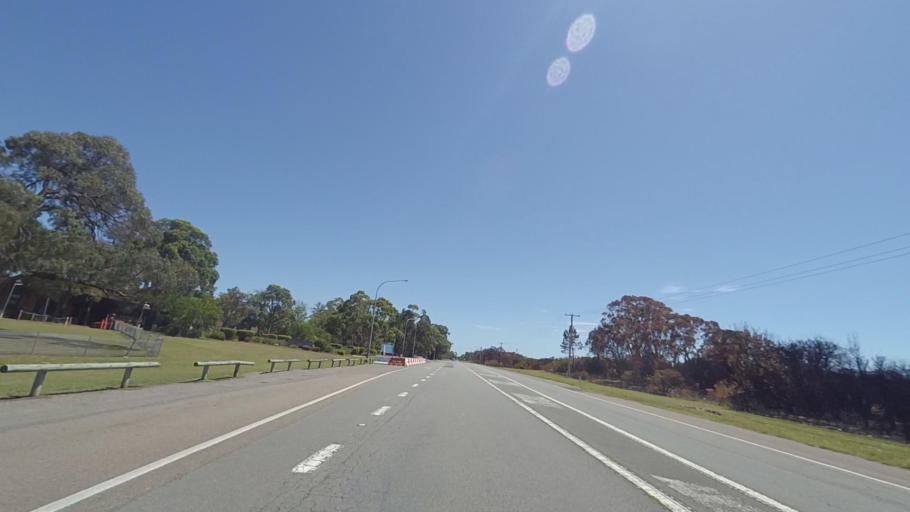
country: AU
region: New South Wales
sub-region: Port Stephens Shire
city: Medowie
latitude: -32.8011
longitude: 151.8515
